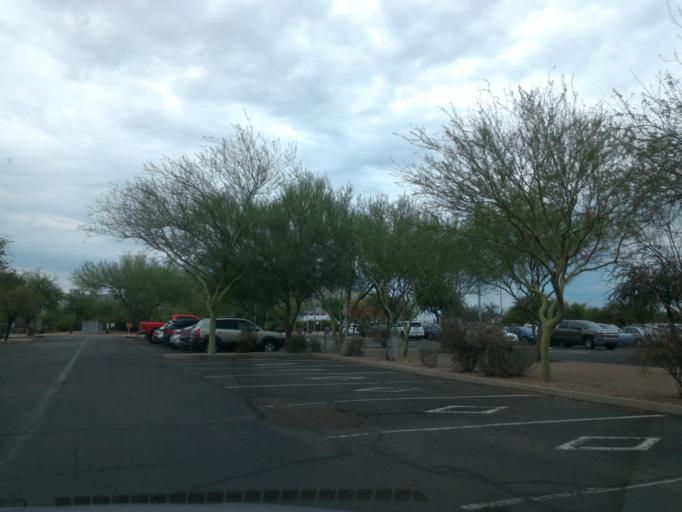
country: US
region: Arizona
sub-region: Maricopa County
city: Sun Lakes
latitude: 33.2429
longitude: -111.8815
